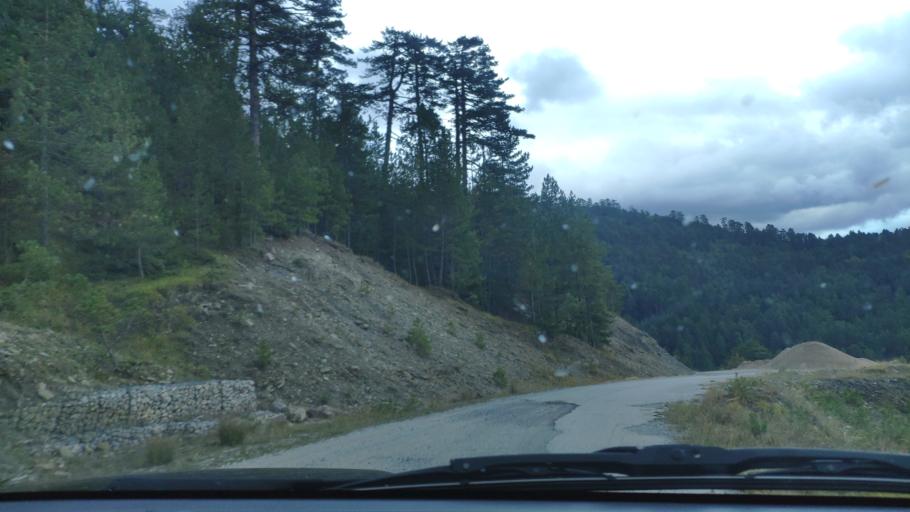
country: AL
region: Korce
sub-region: Rrethi i Kolonjes
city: Erseke
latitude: 40.2898
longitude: 20.8595
